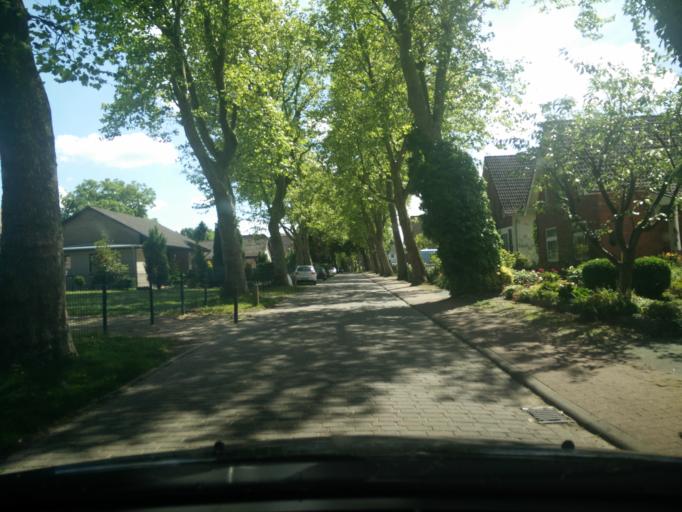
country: DE
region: Schleswig-Holstein
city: Prisdorf
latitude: 53.6779
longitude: 9.7613
